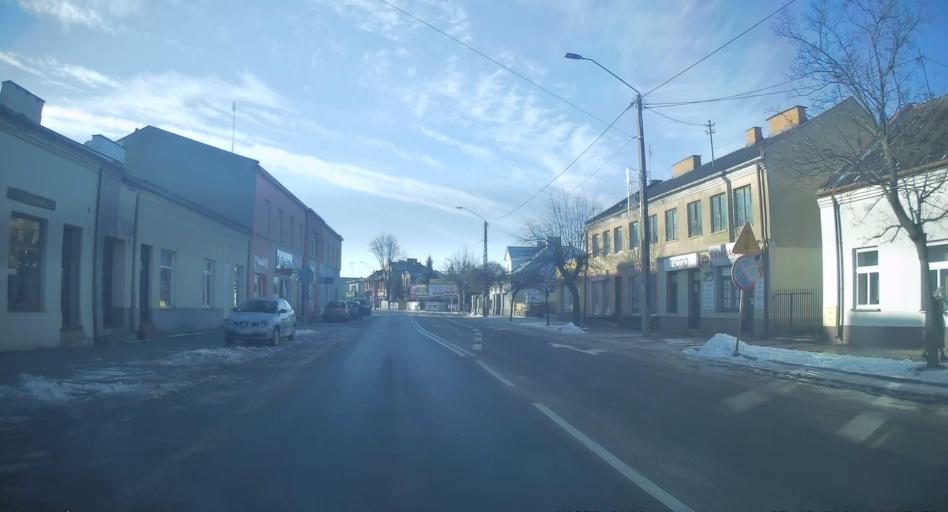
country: PL
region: Lodz Voivodeship
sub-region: Powiat rawski
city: Rawa Mazowiecka
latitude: 51.7635
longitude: 20.2498
